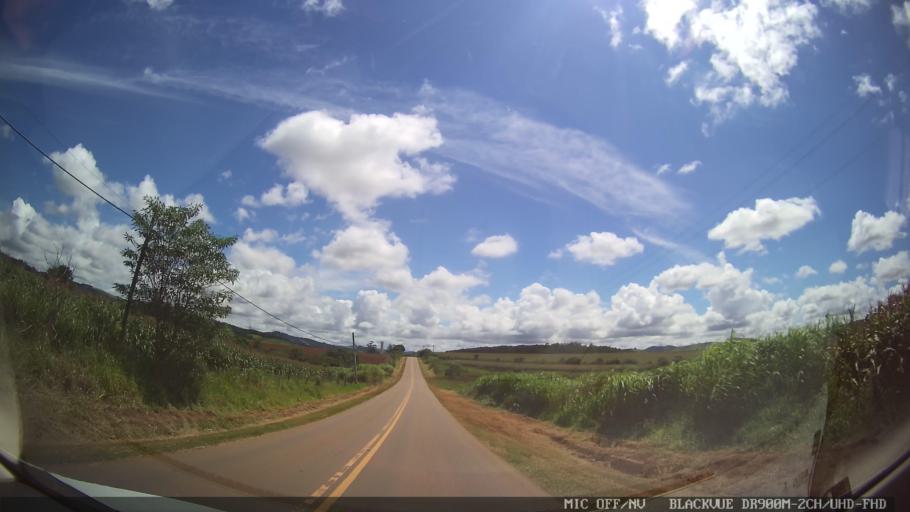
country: BR
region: Sao Paulo
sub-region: Amparo
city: Amparo
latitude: -22.8388
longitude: -46.7062
